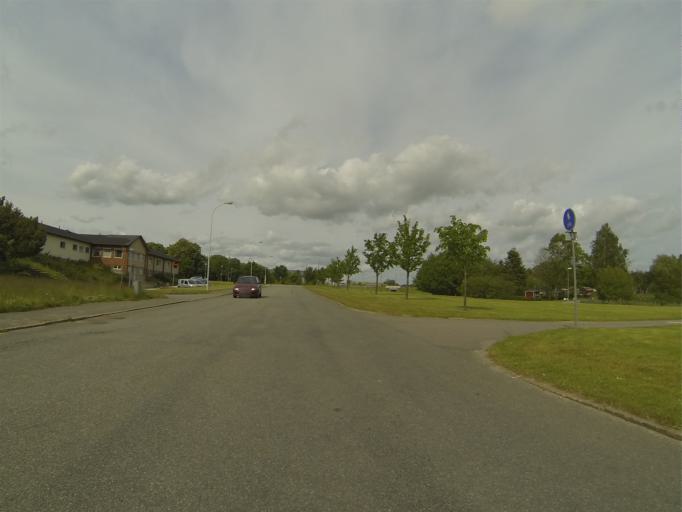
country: SE
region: Skane
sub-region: Tomelilla Kommun
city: Tomelilla
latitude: 55.5466
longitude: 13.9571
